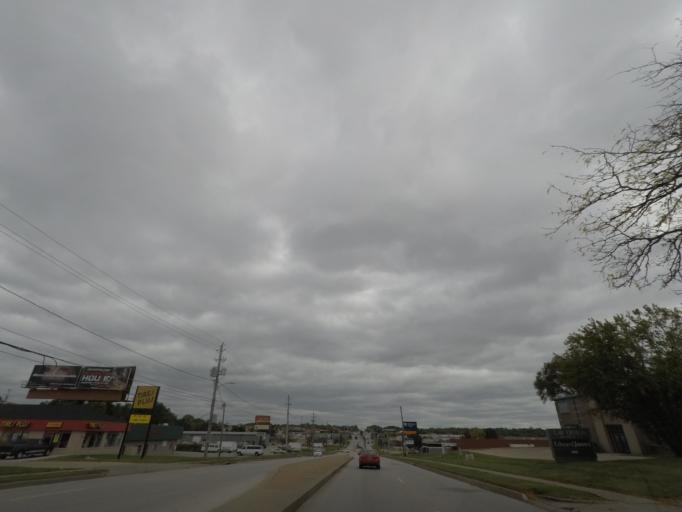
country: US
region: Iowa
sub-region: Polk County
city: Des Moines
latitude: 41.5263
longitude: -93.6058
